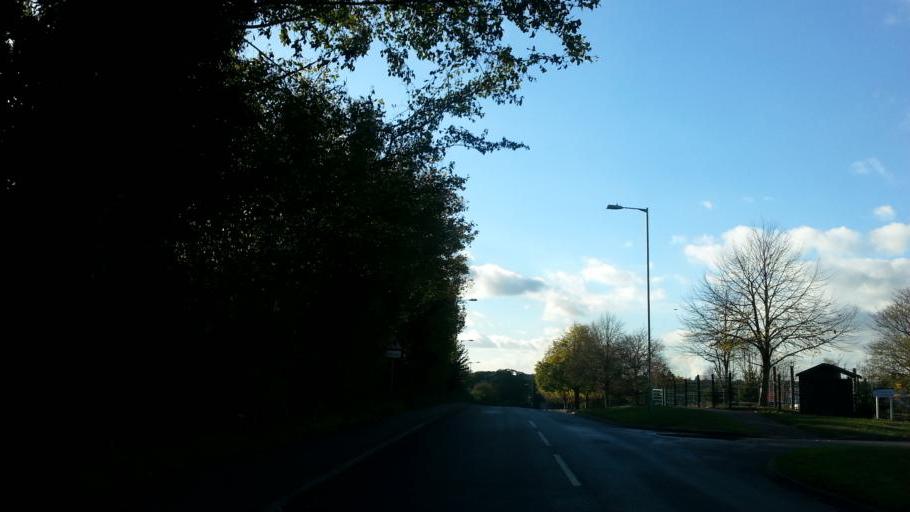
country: GB
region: England
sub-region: Suffolk
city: Thurston
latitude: 52.2538
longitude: 0.8112
